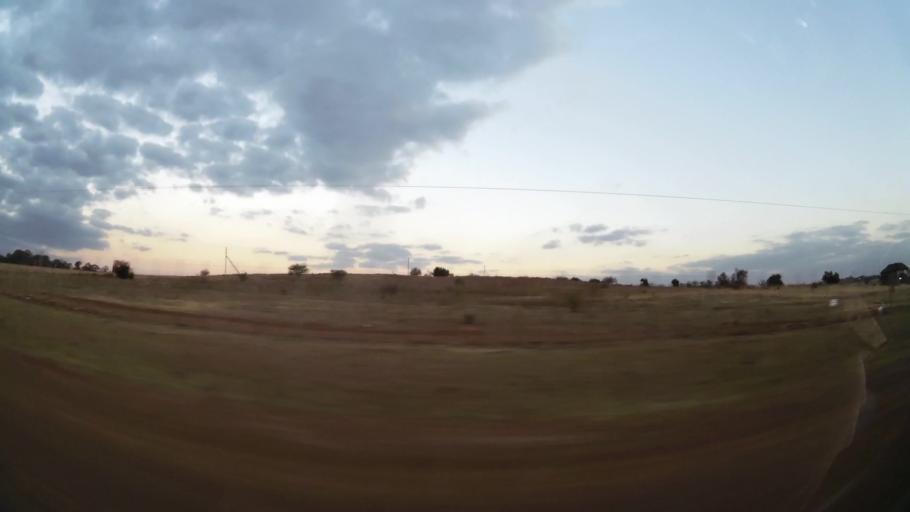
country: ZA
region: Gauteng
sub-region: West Rand District Municipality
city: Krugersdorp
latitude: -26.0614
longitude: 27.6993
